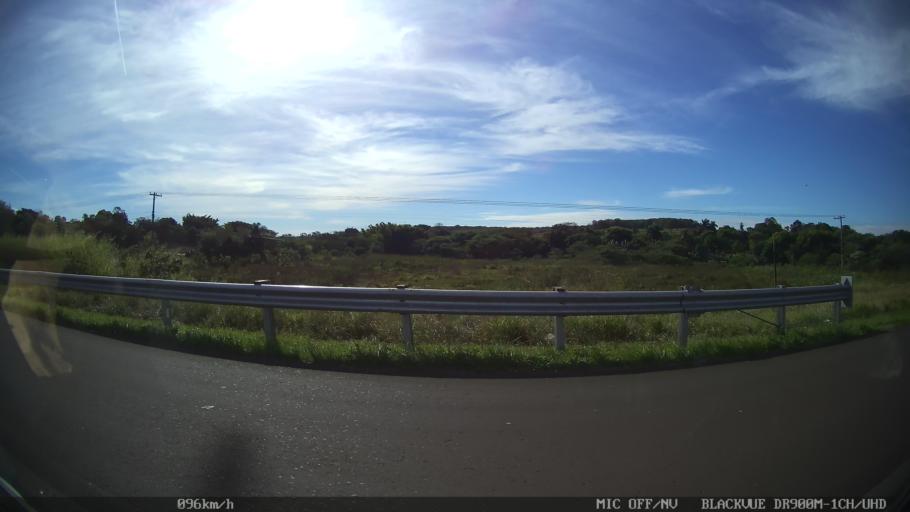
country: BR
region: Sao Paulo
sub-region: Sao Jose Do Rio Preto
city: Sao Jose do Rio Preto
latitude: -20.7964
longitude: -49.3206
